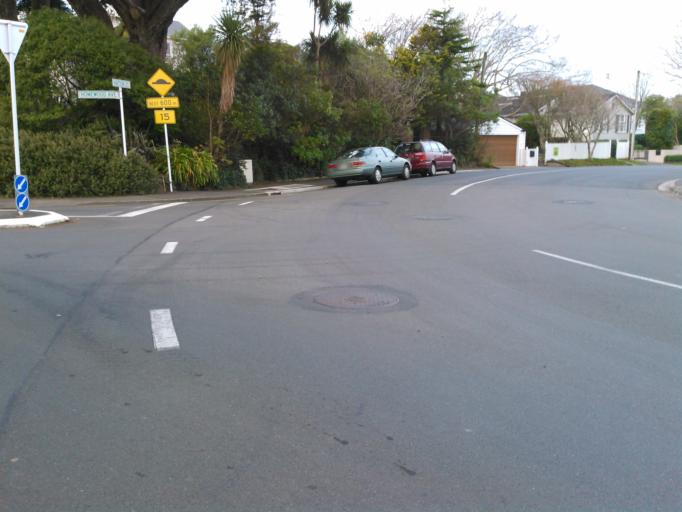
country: NZ
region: Wellington
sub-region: Wellington City
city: Kelburn
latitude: -41.2808
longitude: 174.7436
